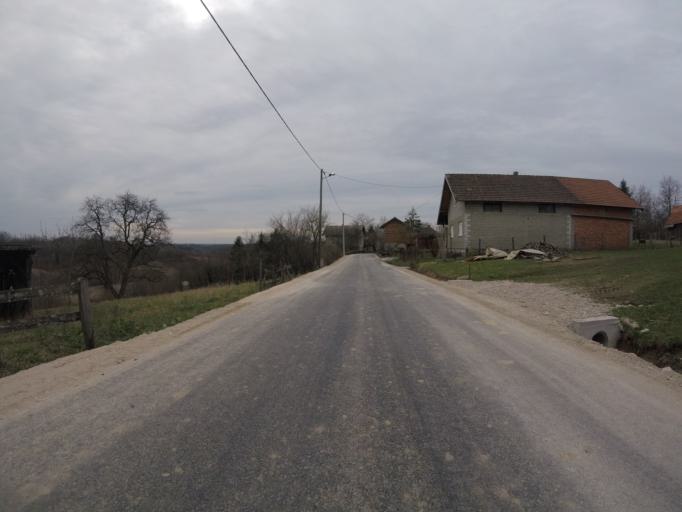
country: HR
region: Grad Zagreb
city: Strmec
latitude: 45.6091
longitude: 15.9107
